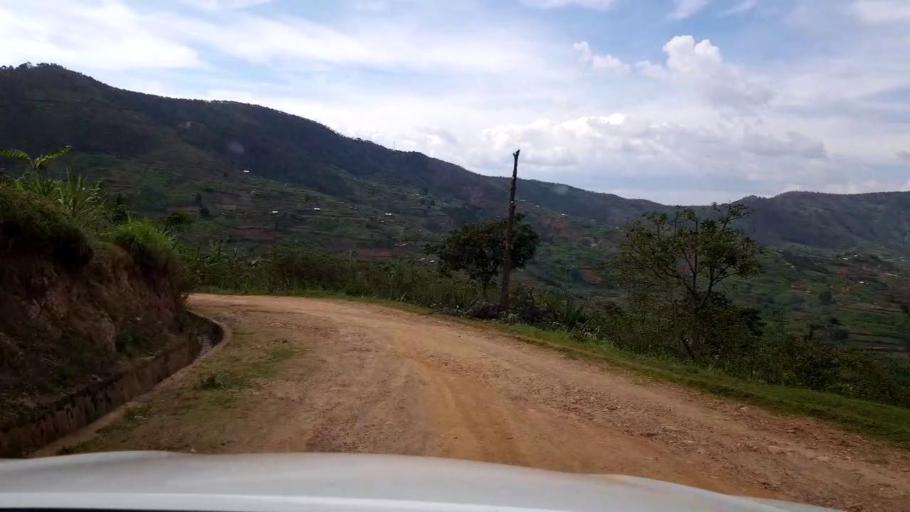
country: RW
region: Southern Province
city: Gitarama
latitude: -1.9816
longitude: 29.7112
